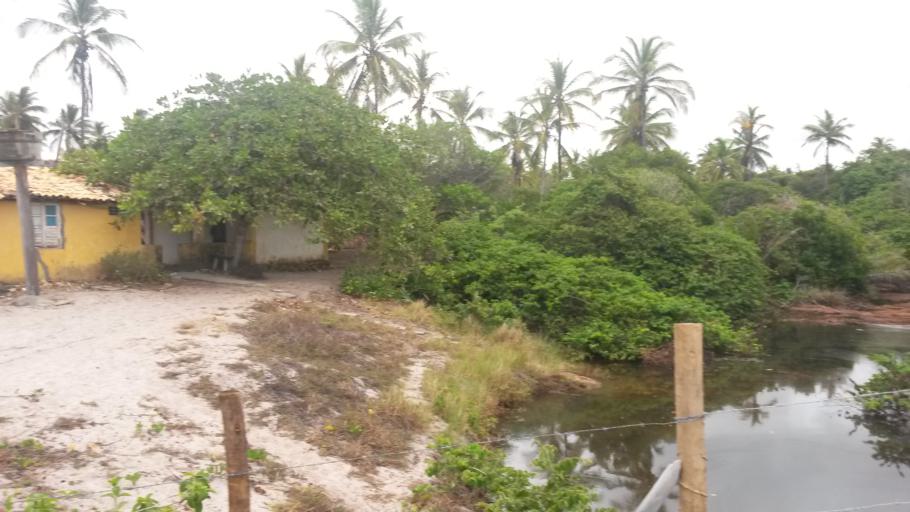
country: BR
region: Bahia
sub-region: Mata De Sao Joao
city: Mata de Sao Joao
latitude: -12.4986
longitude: -37.9614
